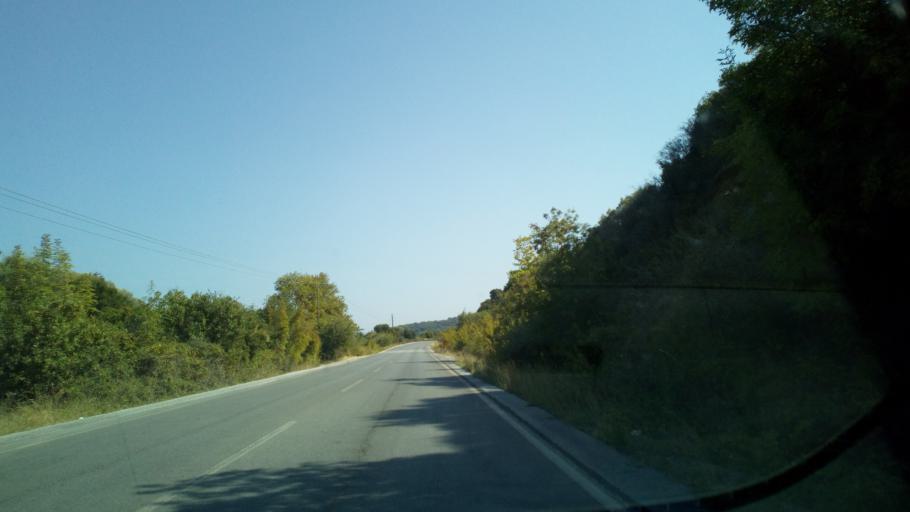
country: GR
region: Central Macedonia
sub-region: Nomos Thessalonikis
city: Stavros
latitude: 40.6457
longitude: 23.7459
